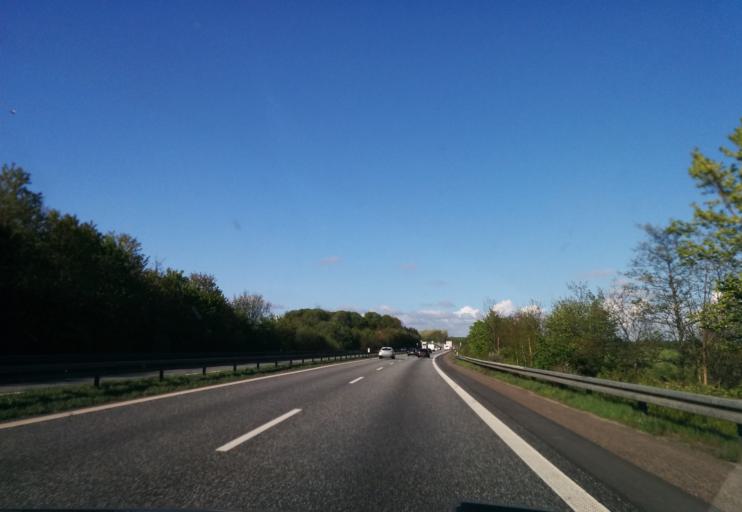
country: DK
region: Central Jutland
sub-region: Horsens Kommune
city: Horsens
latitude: 55.9426
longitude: 9.8207
